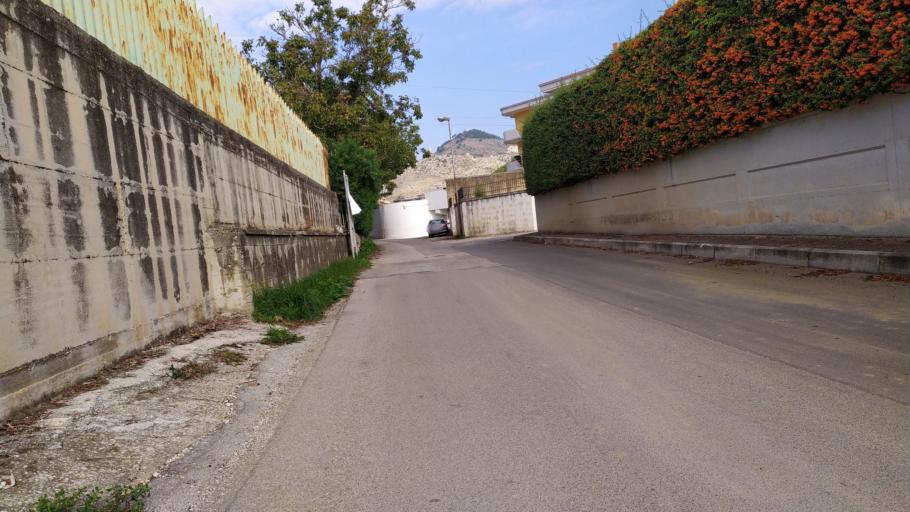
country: IT
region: Campania
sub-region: Provincia di Caserta
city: Maddaloni
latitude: 41.0284
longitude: 14.3966
